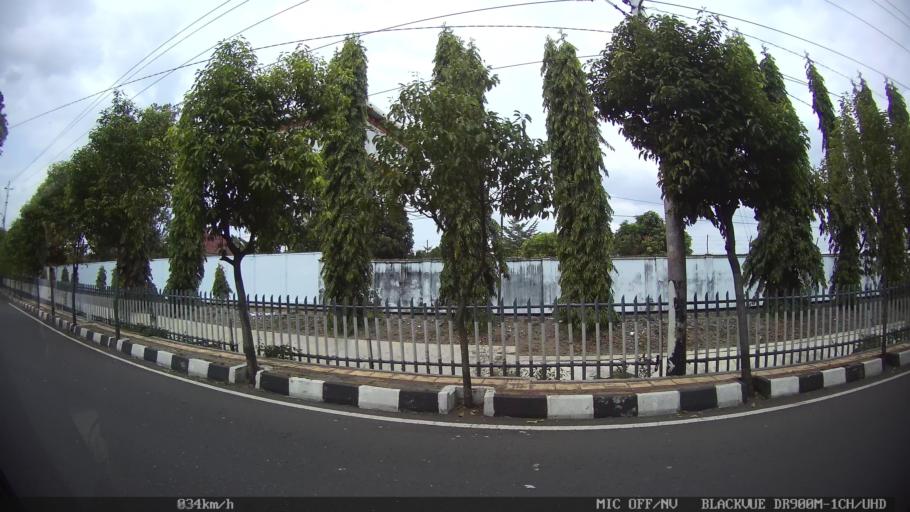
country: ID
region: Daerah Istimewa Yogyakarta
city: Yogyakarta
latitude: -7.7873
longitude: 110.3815
